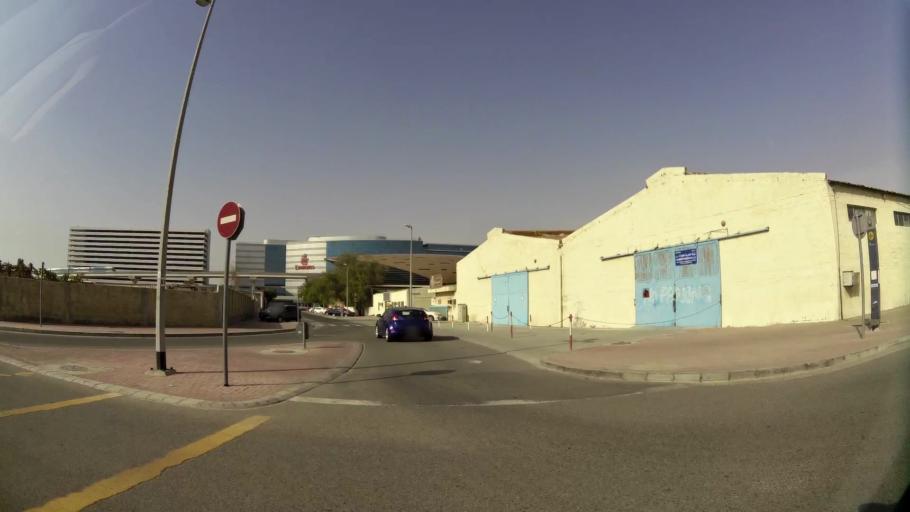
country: AE
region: Ash Shariqah
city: Sharjah
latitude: 25.2396
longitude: 55.3639
